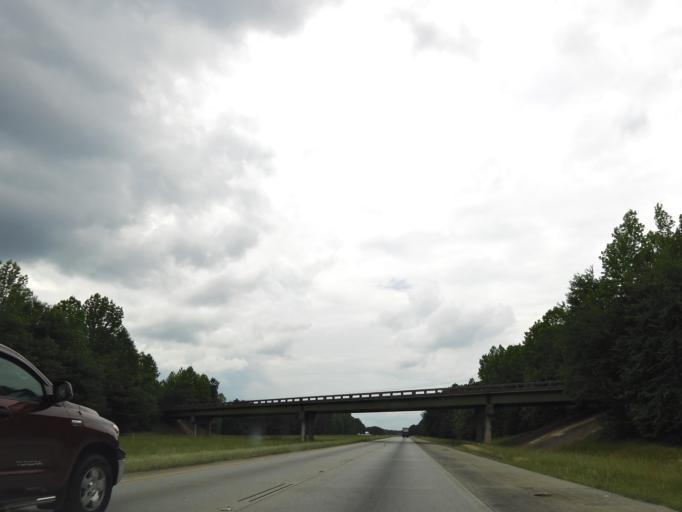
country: US
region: Georgia
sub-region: Carroll County
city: Villa Rica
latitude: 33.7177
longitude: -84.9746
